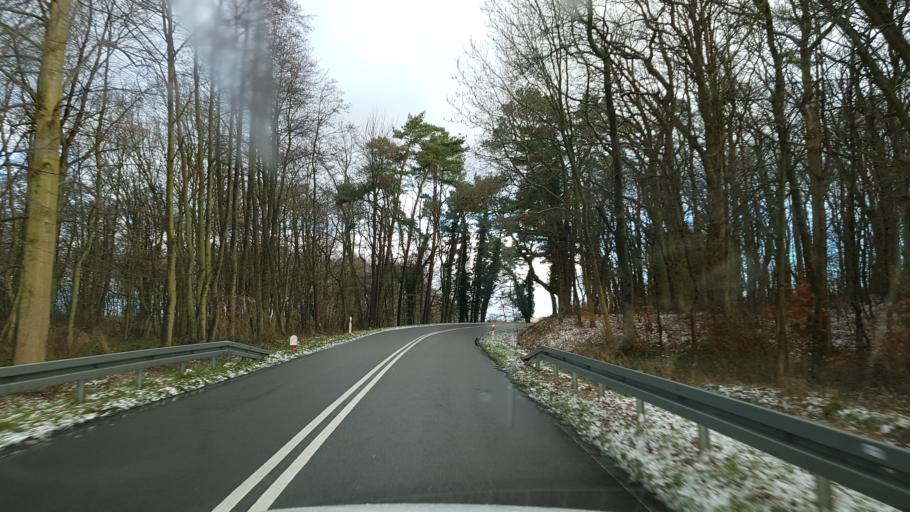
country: PL
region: West Pomeranian Voivodeship
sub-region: Powiat gryficki
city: Karnice
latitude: 54.0438
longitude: 15.0614
